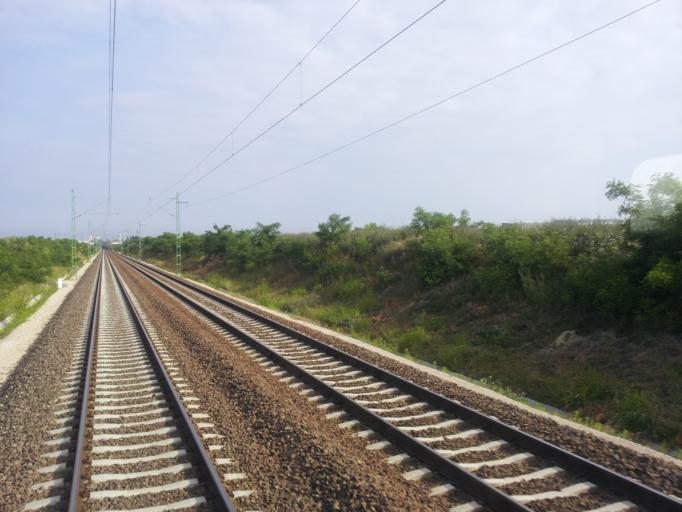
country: HU
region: Fejer
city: Szekesfehervar
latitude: 47.1759
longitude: 18.4572
